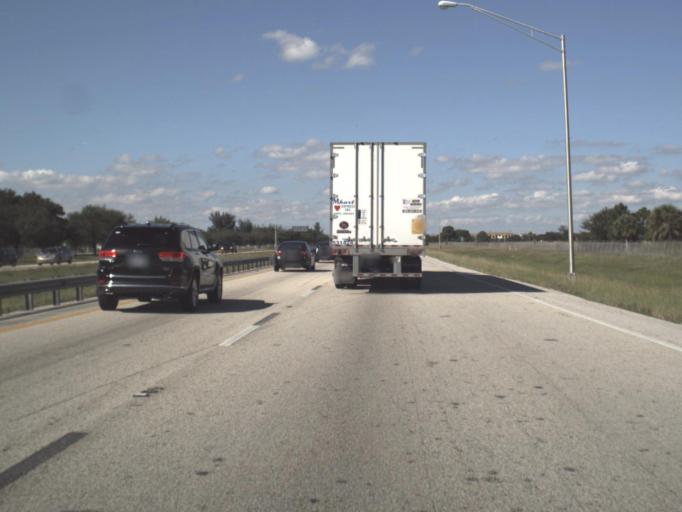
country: US
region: Florida
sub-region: Miami-Dade County
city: Lake Lucerne
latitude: 25.9723
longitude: -80.2534
